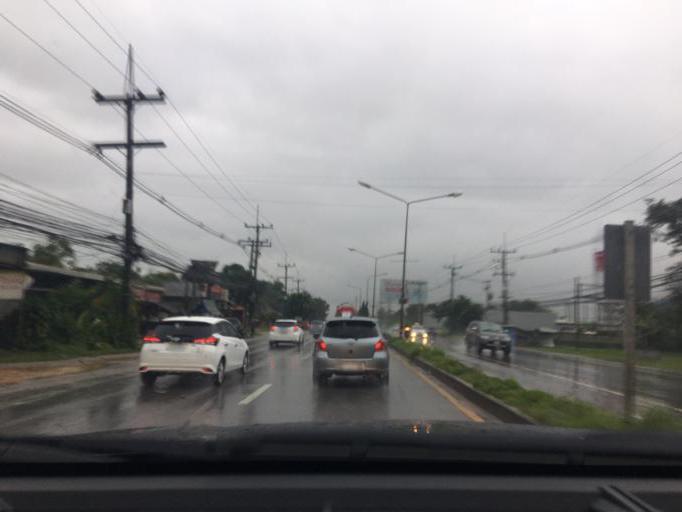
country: TH
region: Chiang Rai
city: Chiang Rai
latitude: 20.0167
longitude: 99.8700
